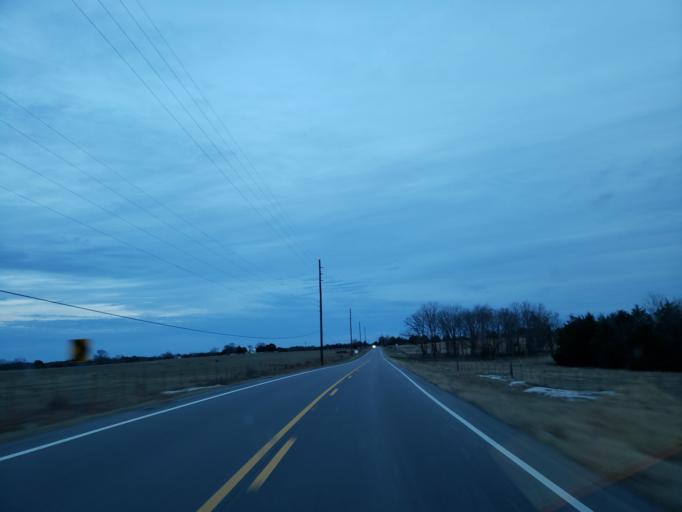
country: US
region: Alabama
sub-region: Sumter County
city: Livingston
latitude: 32.8126
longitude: -88.2780
